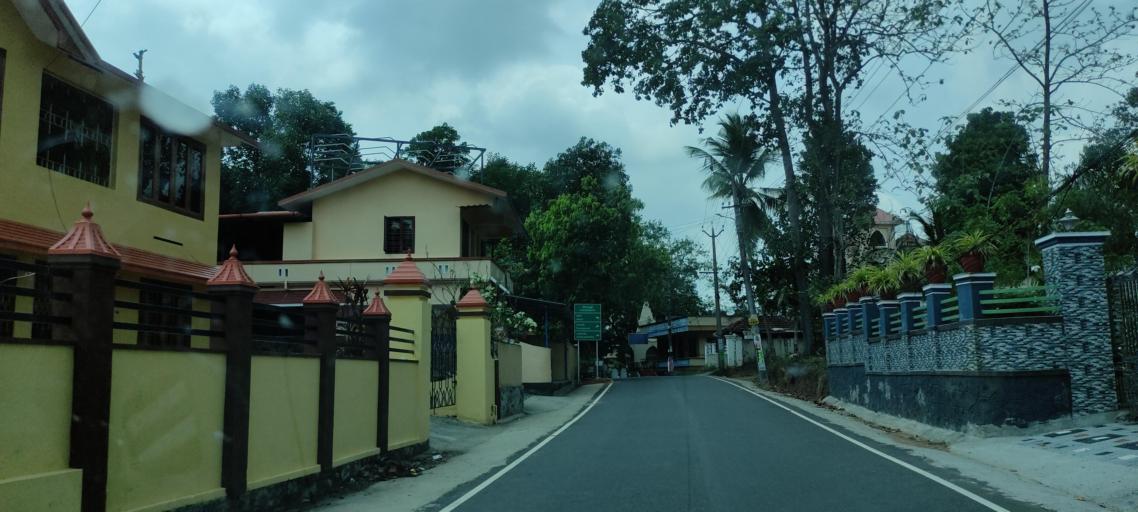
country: IN
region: Kerala
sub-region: Pattanamtitta
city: Adur
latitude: 9.1749
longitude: 76.7430
